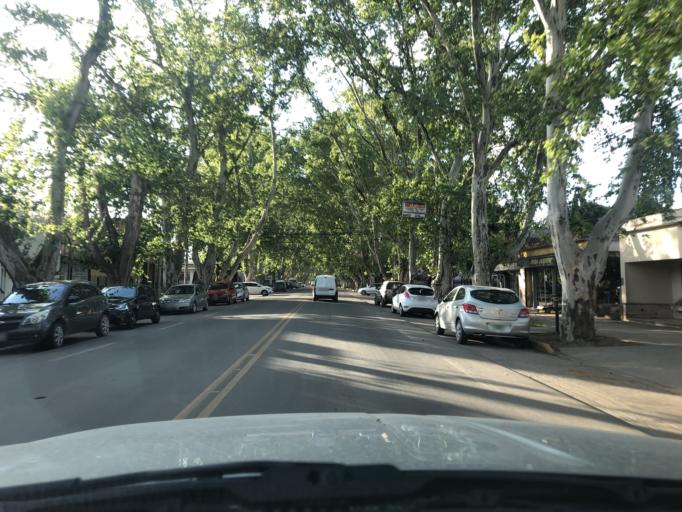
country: AR
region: Cordoba
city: Jesus Maria
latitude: -31.0192
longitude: -64.0642
